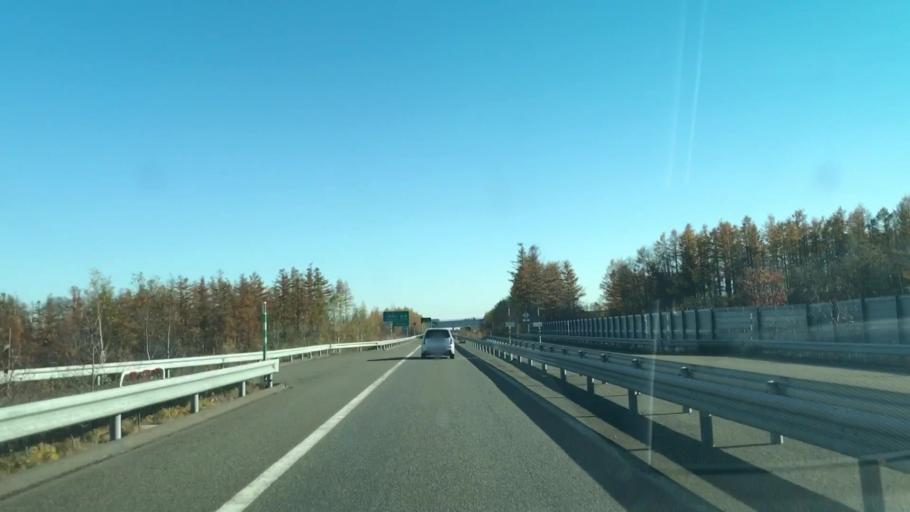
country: JP
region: Hokkaido
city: Otofuke
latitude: 43.0011
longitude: 142.8491
